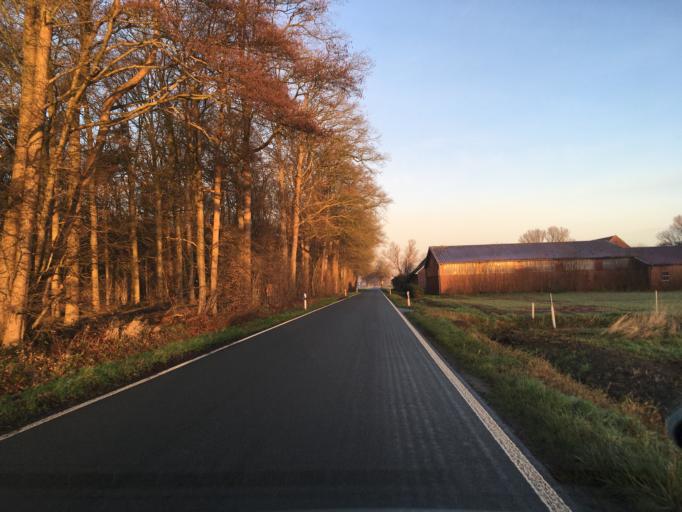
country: DE
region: North Rhine-Westphalia
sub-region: Regierungsbezirk Munster
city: Schoppingen
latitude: 52.0468
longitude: 7.2386
